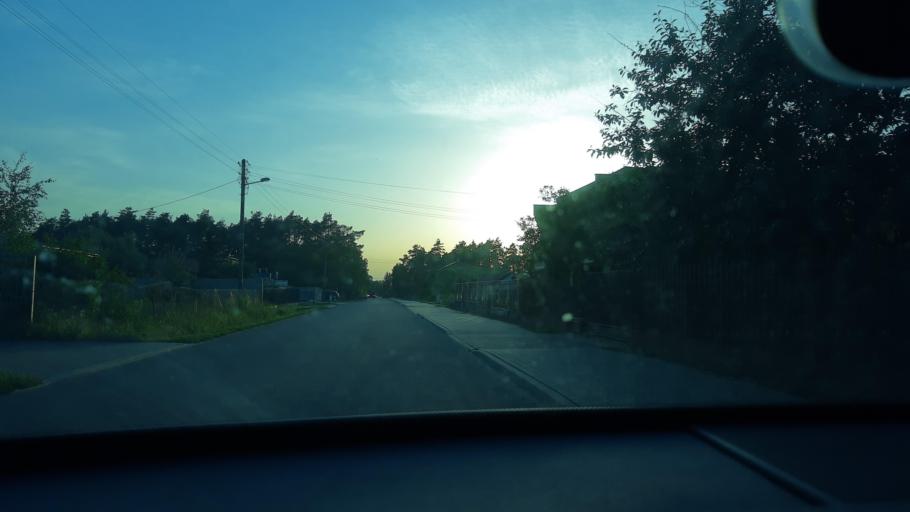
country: PL
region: Lodz Voivodeship
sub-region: Powiat zdunskowolski
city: Zdunska Wola
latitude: 51.6074
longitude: 18.9835
